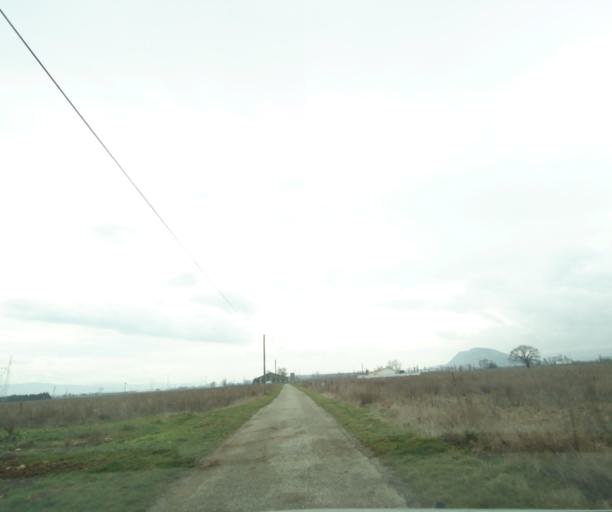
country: FR
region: Rhone-Alpes
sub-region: Departement de l'Ardeche
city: Cornas
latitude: 44.9777
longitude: 4.8703
